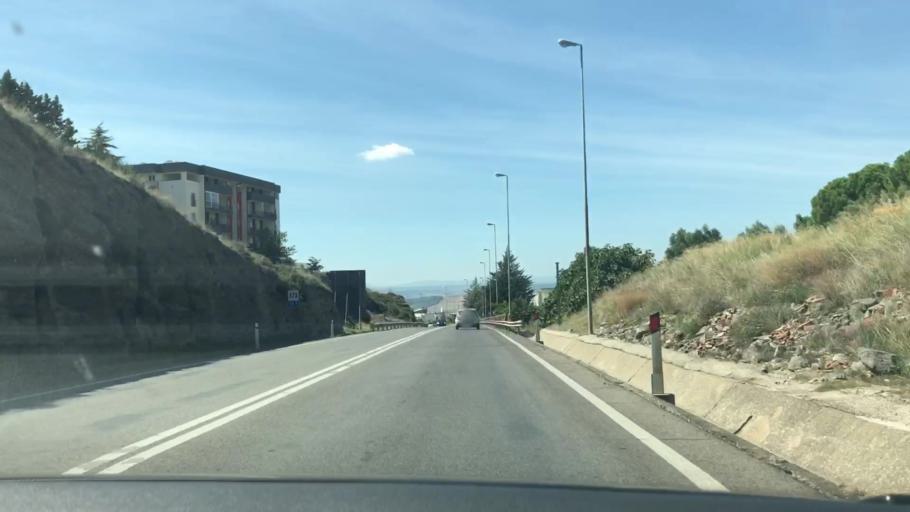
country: IT
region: Basilicate
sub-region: Provincia di Matera
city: Matera
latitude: 40.6762
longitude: 16.5805
